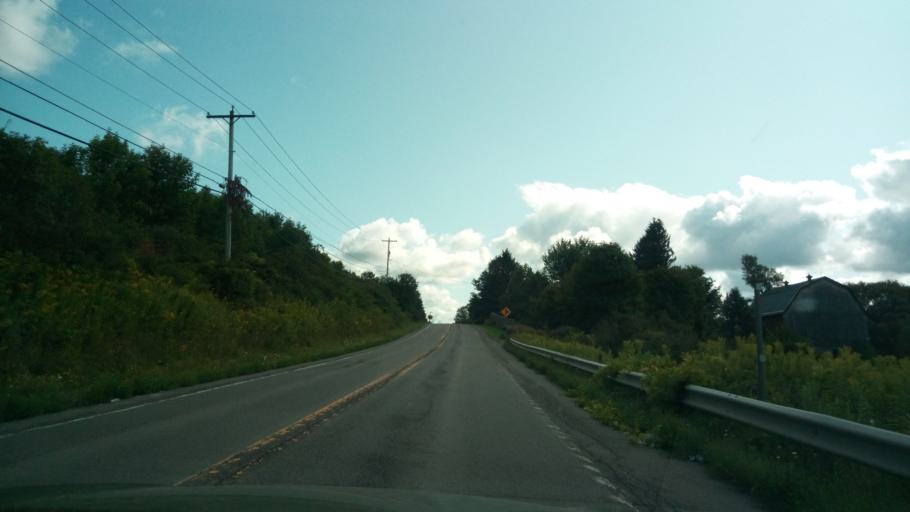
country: US
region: New York
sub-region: Onondaga County
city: Nedrow
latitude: 42.8027
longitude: -76.0976
